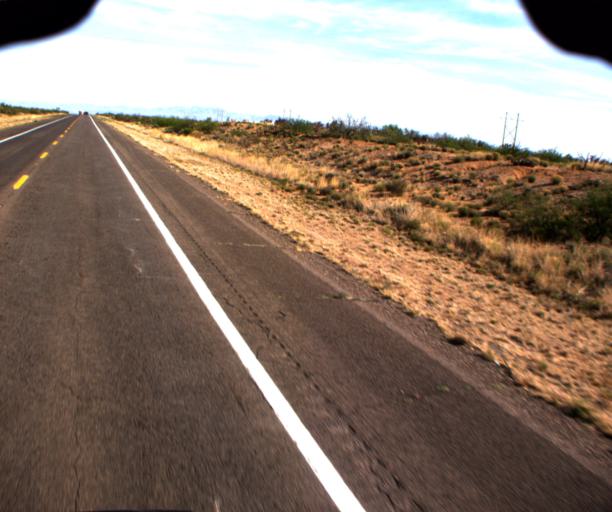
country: US
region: Arizona
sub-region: Graham County
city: Swift Trail Junction
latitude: 32.6187
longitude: -109.6887
